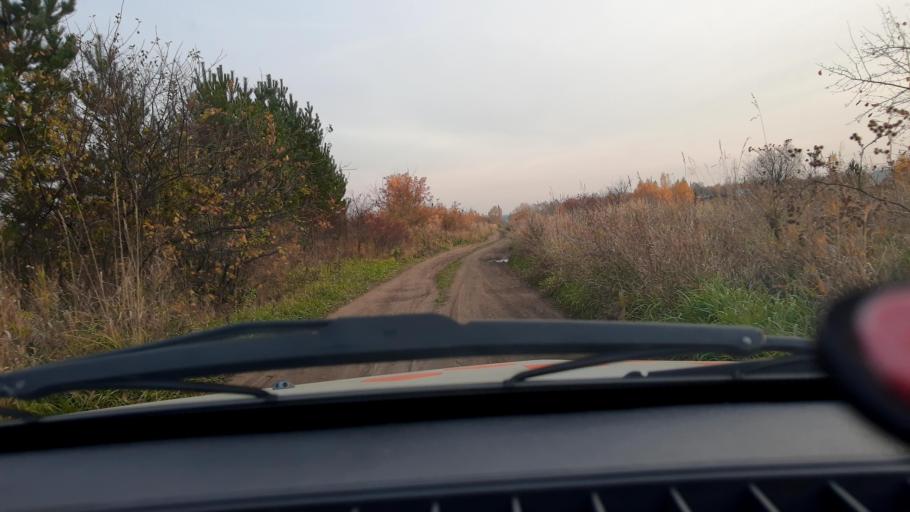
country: RU
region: Bashkortostan
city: Iglino
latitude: 54.8025
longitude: 56.3470
